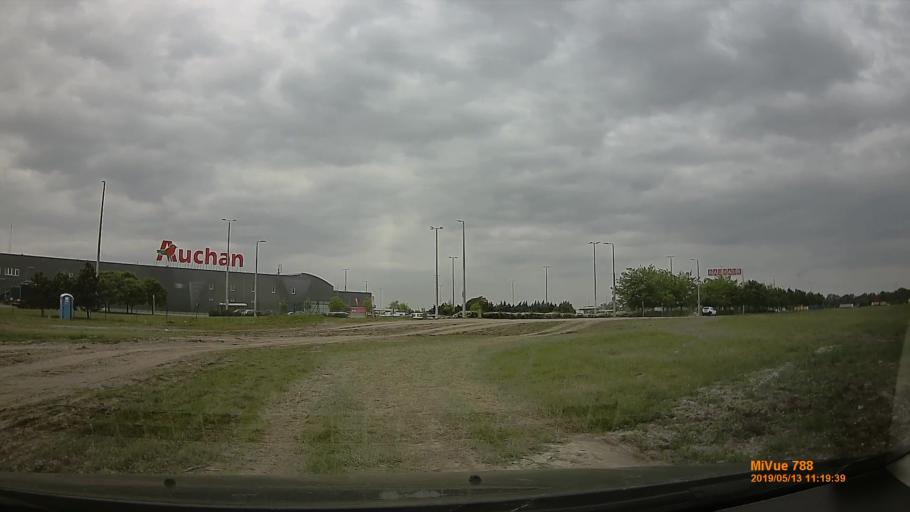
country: HU
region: Pest
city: Szigetszentmiklos
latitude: 47.3825
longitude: 19.0297
